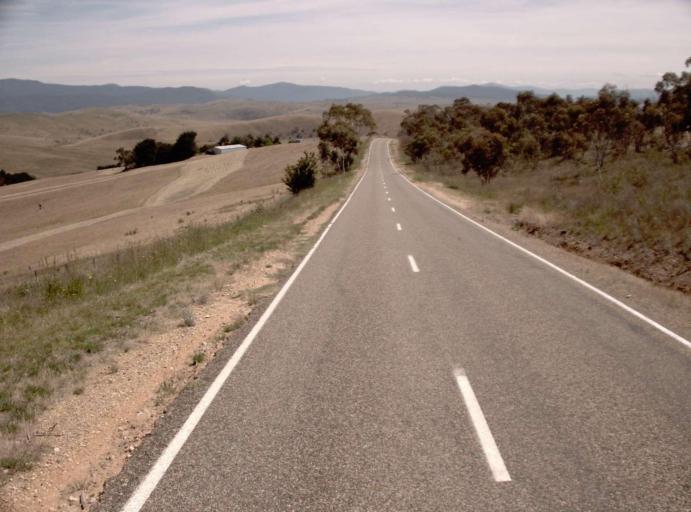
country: AU
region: Victoria
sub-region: Alpine
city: Mount Beauty
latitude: -37.0254
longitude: 147.6502
